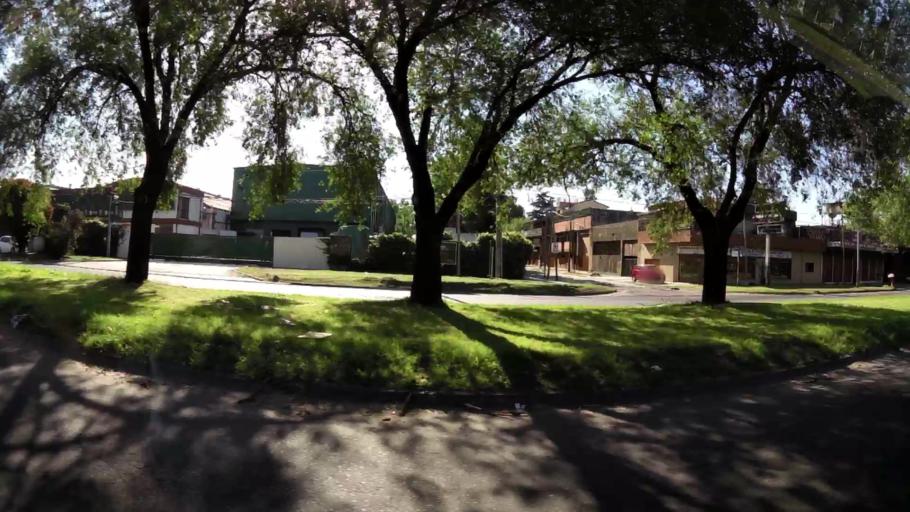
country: AR
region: Buenos Aires
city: Caseros
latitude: -34.5660
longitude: -58.5896
